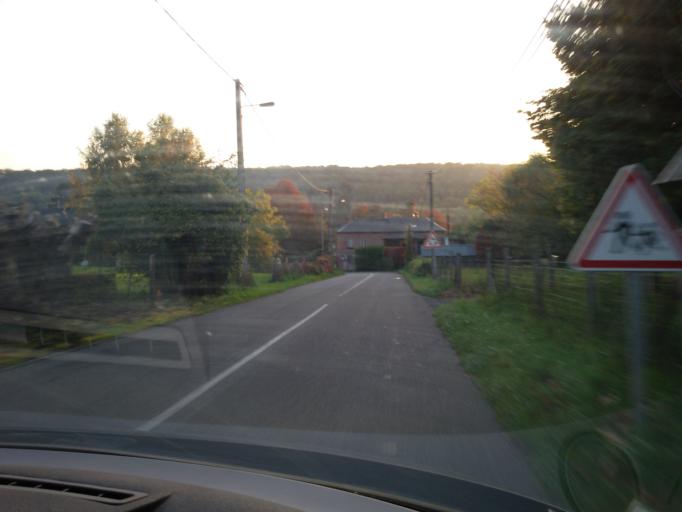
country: FR
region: Lower Normandy
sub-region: Departement du Calvados
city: Ablon
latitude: 49.4111
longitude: 0.3028
